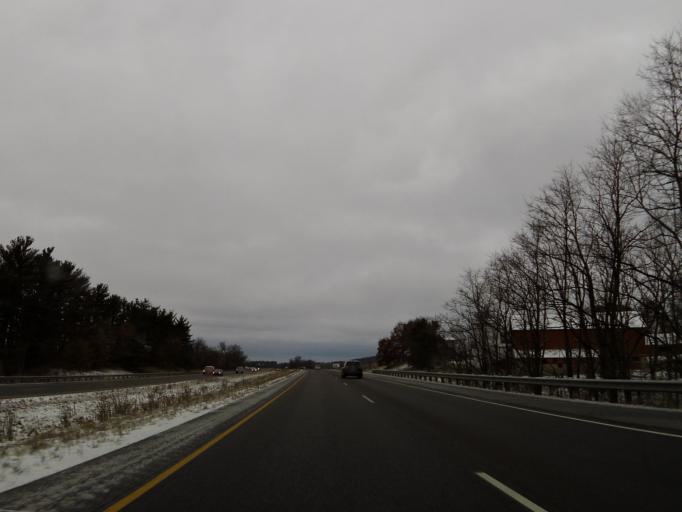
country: US
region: Wisconsin
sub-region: Eau Claire County
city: Fall Creek
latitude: 44.7202
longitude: -91.3517
